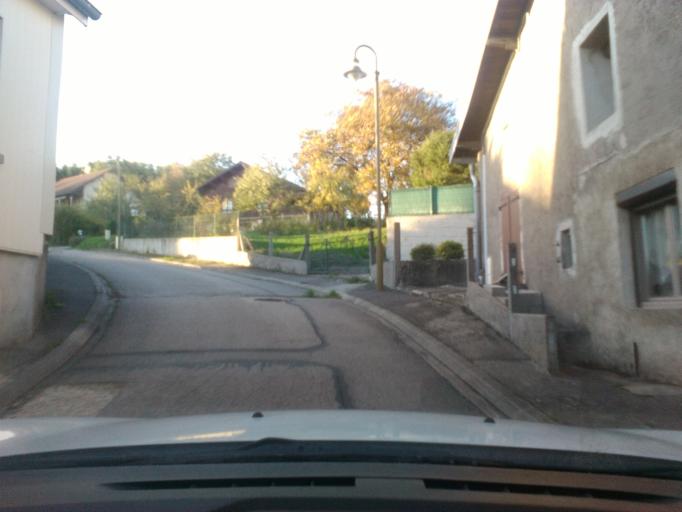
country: FR
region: Lorraine
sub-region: Departement des Vosges
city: Charmes
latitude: 48.3363
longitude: 6.2733
